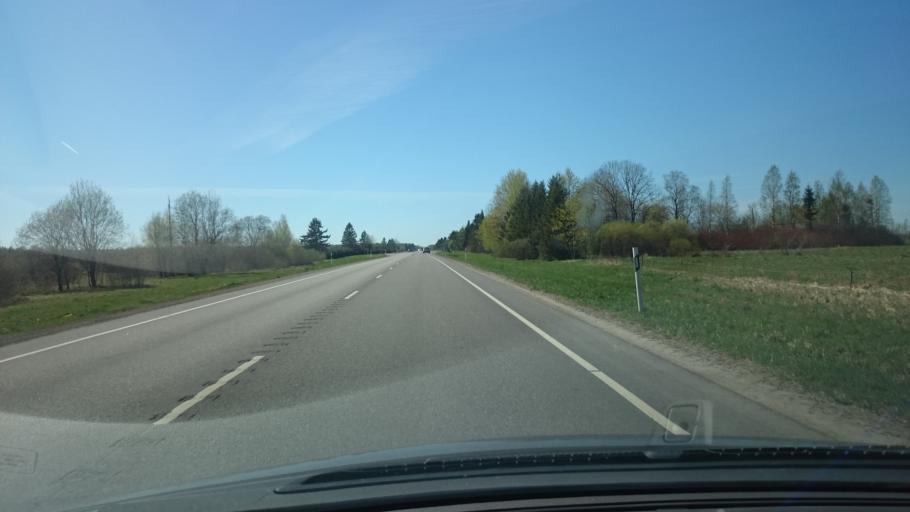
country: EE
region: Ida-Virumaa
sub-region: Sillamaee linn
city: Sillamae
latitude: 59.3918
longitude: 27.6961
